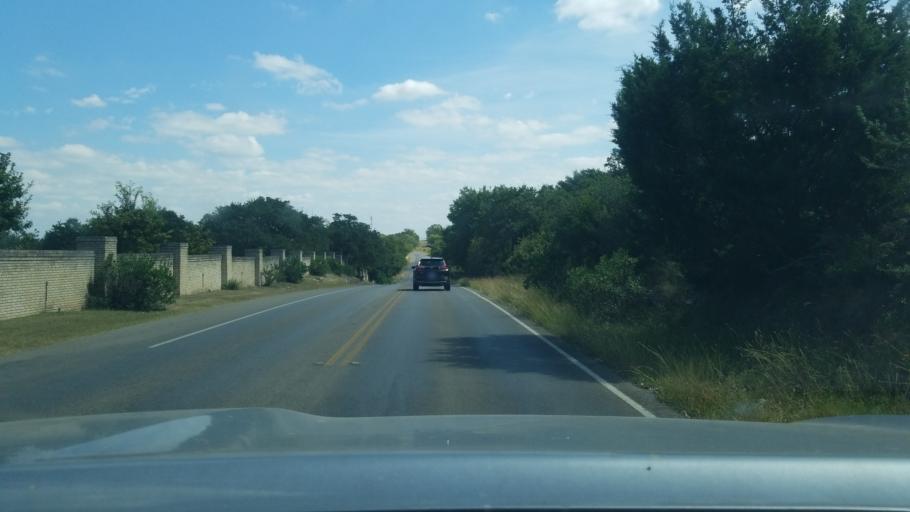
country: US
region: Texas
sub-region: Bexar County
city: Fair Oaks Ranch
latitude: 29.7311
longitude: -98.6395
